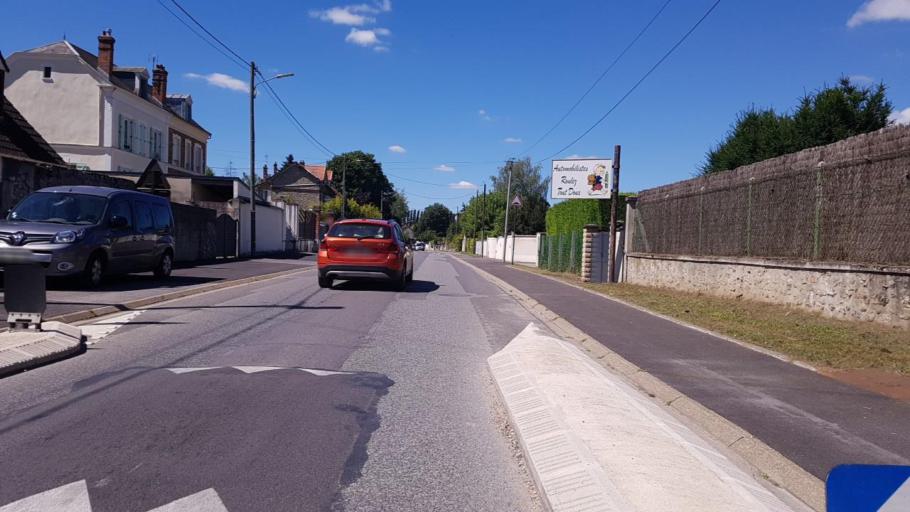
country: FR
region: Ile-de-France
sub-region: Departement de Seine-et-Marne
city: Chamigny
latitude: 48.9622
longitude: 3.1487
